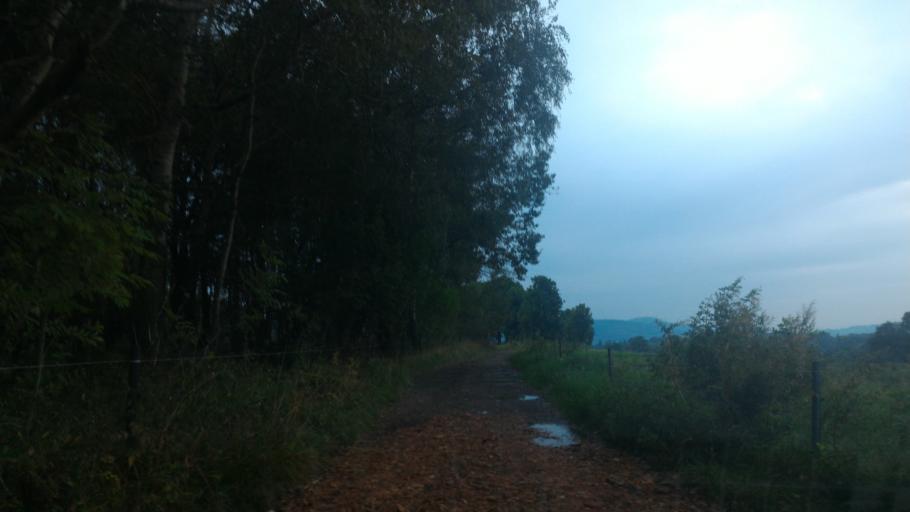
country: CZ
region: Ustecky
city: Dolni Podluzi
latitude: 50.8981
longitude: 14.5641
